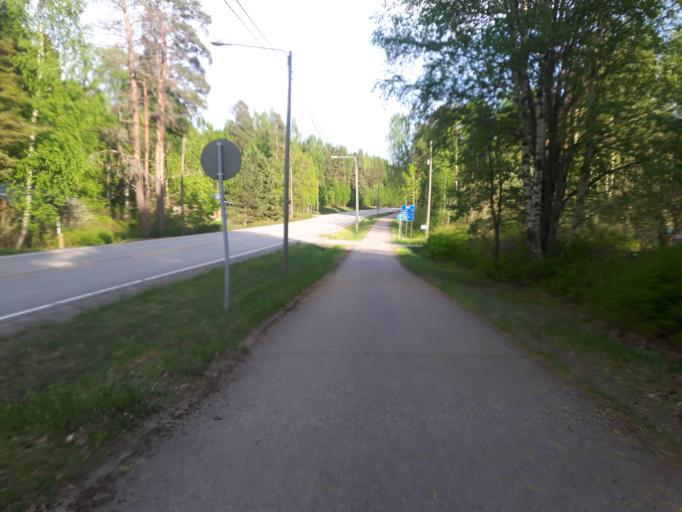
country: FI
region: Uusimaa
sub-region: Loviisa
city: Perna
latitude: 60.4964
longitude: 25.9660
